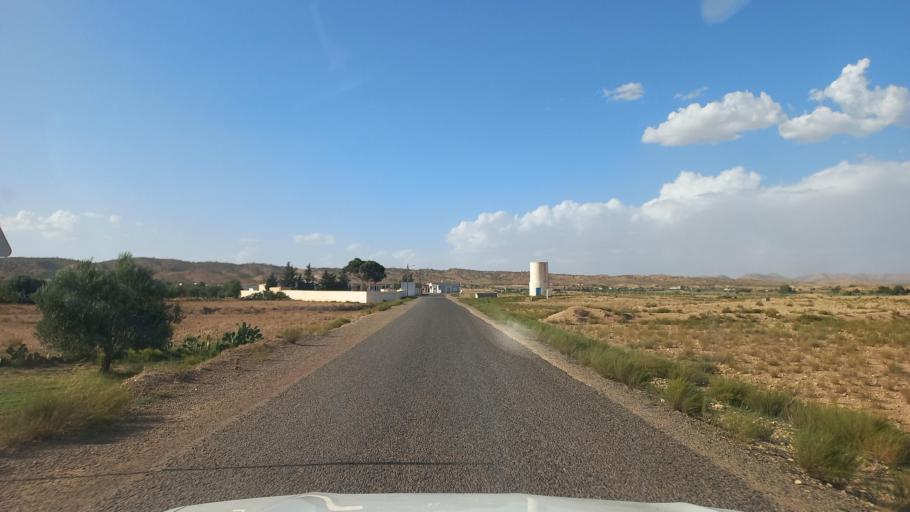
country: TN
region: Al Qasrayn
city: Sbiba
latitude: 35.3425
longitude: 8.9913
